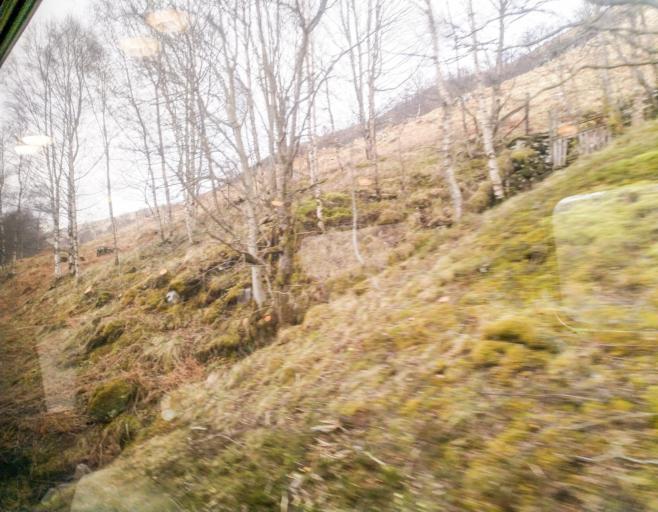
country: GB
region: Scotland
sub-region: Highland
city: Spean Bridge
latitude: 56.7890
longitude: -4.7287
